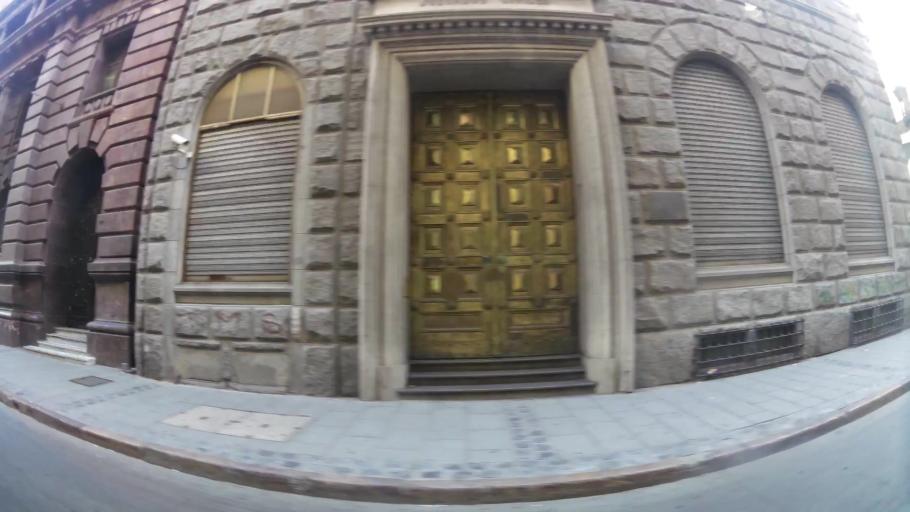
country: CL
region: Valparaiso
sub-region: Provincia de Valparaiso
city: Valparaiso
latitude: -33.0399
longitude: -71.6276
